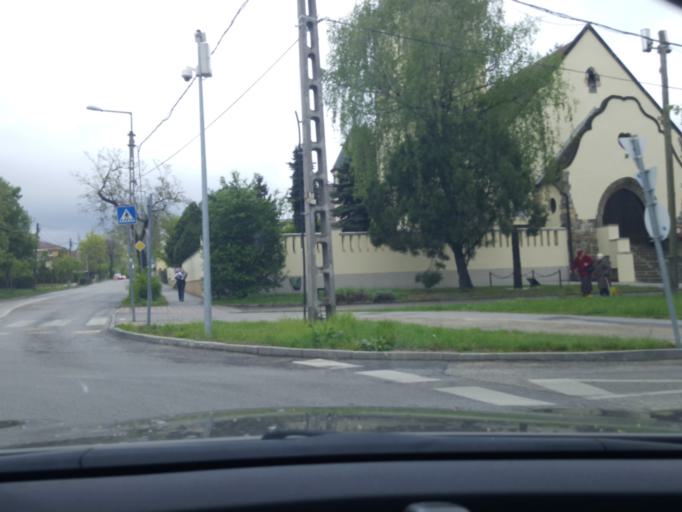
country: HU
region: Budapest
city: Budapest X. keruelet
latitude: 47.4799
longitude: 19.1410
